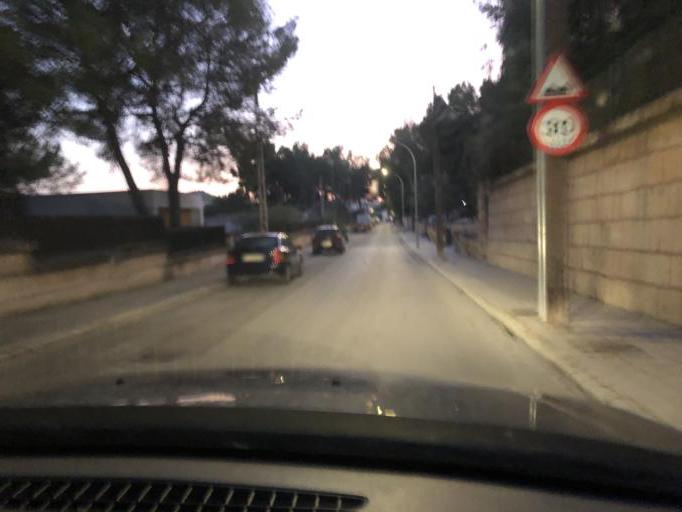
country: ES
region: Balearic Islands
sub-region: Illes Balears
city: Santa Ponsa
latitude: 39.5229
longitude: 2.4898
